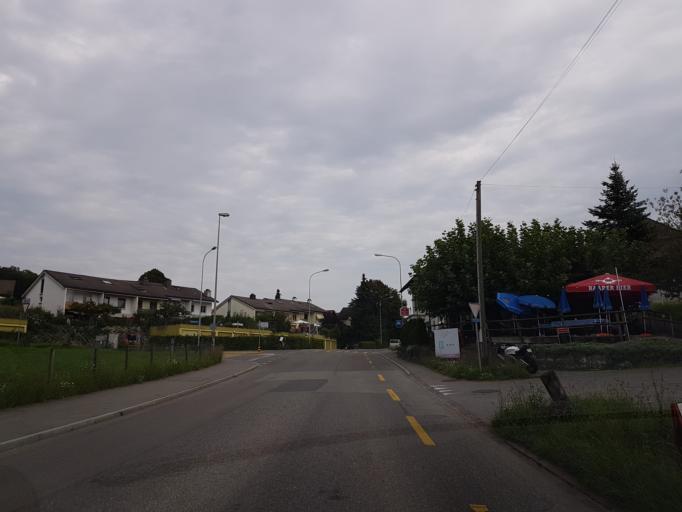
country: CH
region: Zurich
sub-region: Bezirk Affoltern
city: Obfelden / Oberlunnern
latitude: 47.2641
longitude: 8.4073
